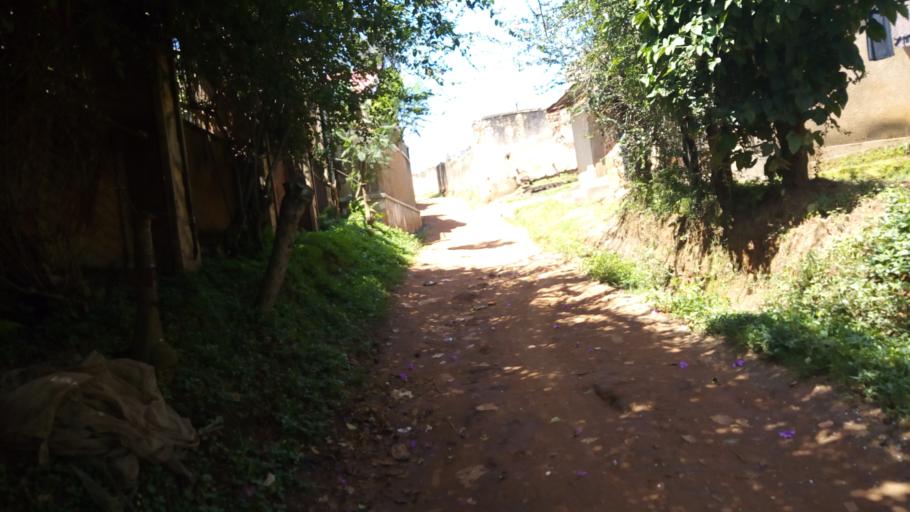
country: UG
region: Central Region
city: Kampala Central Division
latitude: 0.3591
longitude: 32.5574
